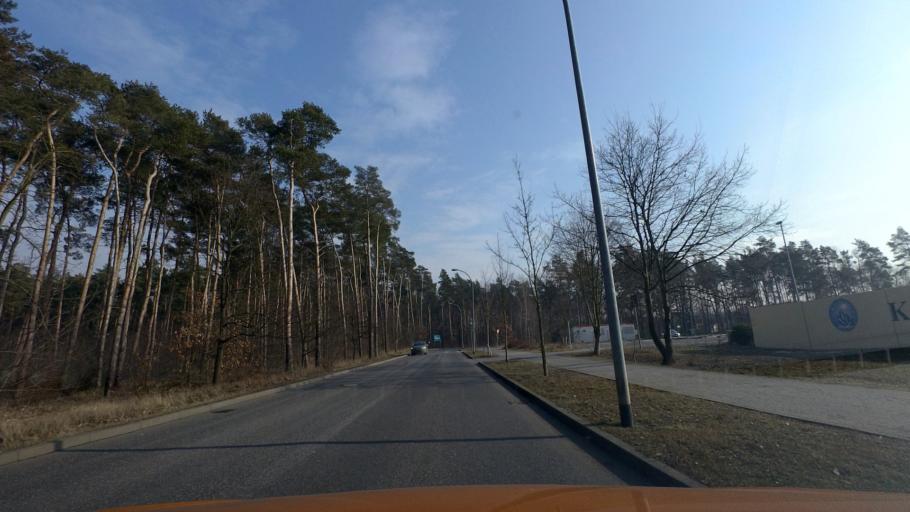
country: DE
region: Brandenburg
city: Ludwigsfelde
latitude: 52.3068
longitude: 13.2625
